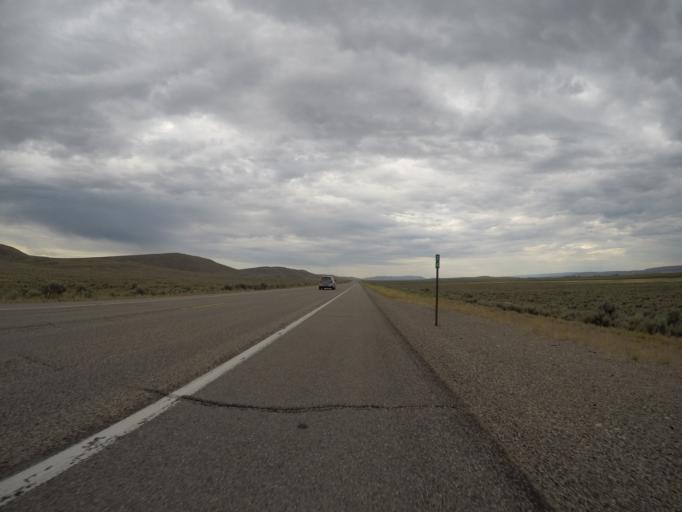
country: US
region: Utah
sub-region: Rich County
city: Randolph
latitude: 41.8983
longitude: -110.9591
